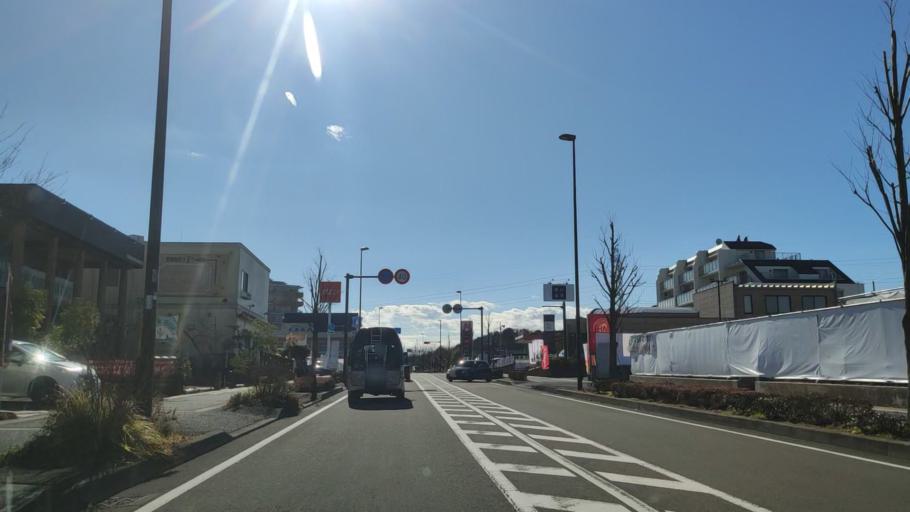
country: JP
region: Tokyo
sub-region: Machida-shi
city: Machida
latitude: 35.5213
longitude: 139.4979
